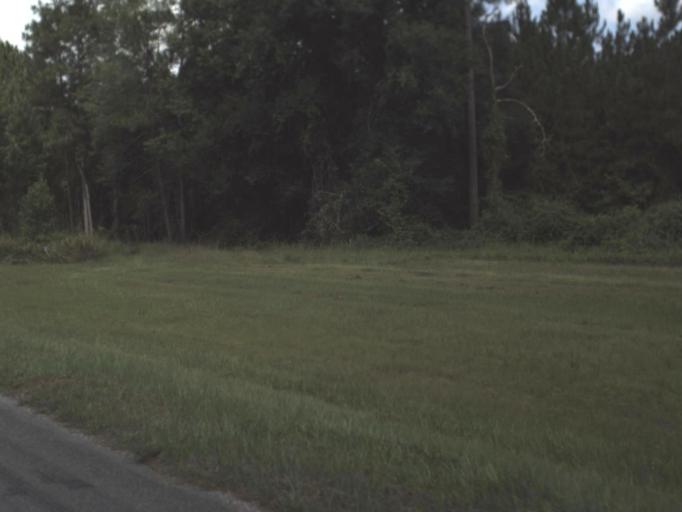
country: US
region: Florida
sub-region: Union County
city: Lake Butler
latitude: 30.0498
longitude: -82.2655
